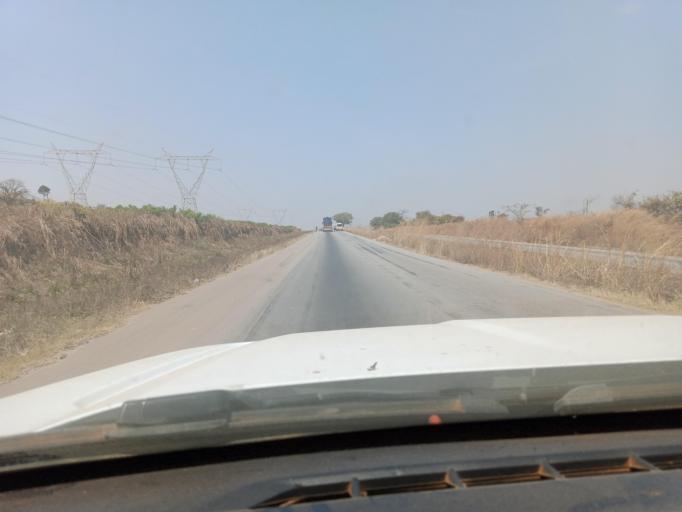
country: ZM
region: Copperbelt
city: Luanshya
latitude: -12.9636
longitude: 28.3940
